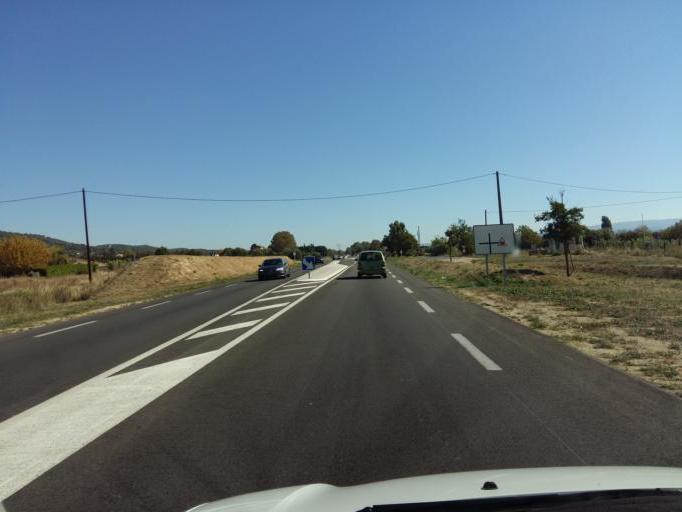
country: FR
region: Provence-Alpes-Cote d'Azur
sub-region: Departement du Vaucluse
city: Villelaure
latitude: 43.7114
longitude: 5.4177
